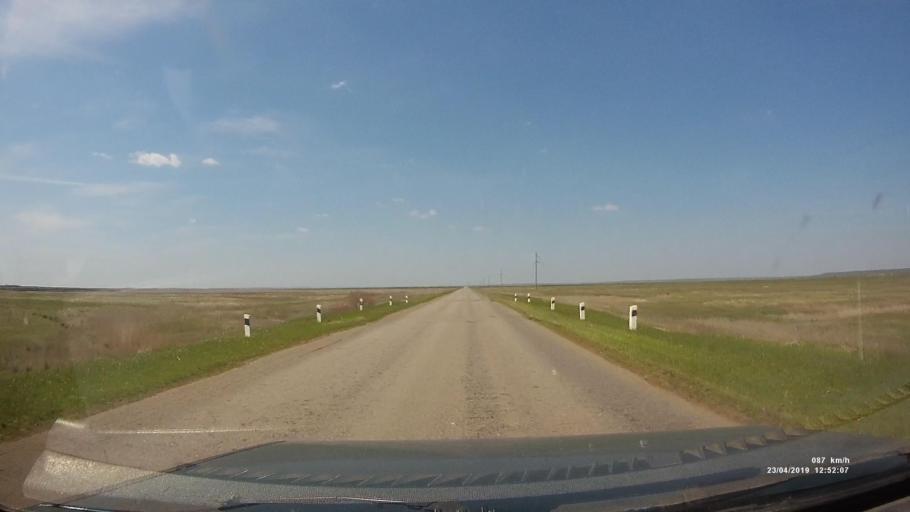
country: RU
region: Kalmykiya
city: Yashalta
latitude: 46.5615
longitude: 42.6138
